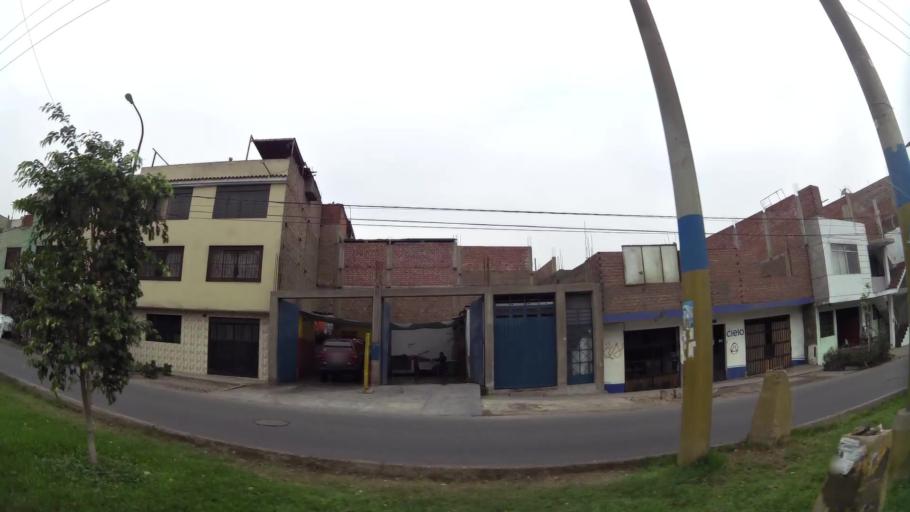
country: PE
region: Lima
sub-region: Lima
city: Independencia
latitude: -11.9637
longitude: -76.9943
